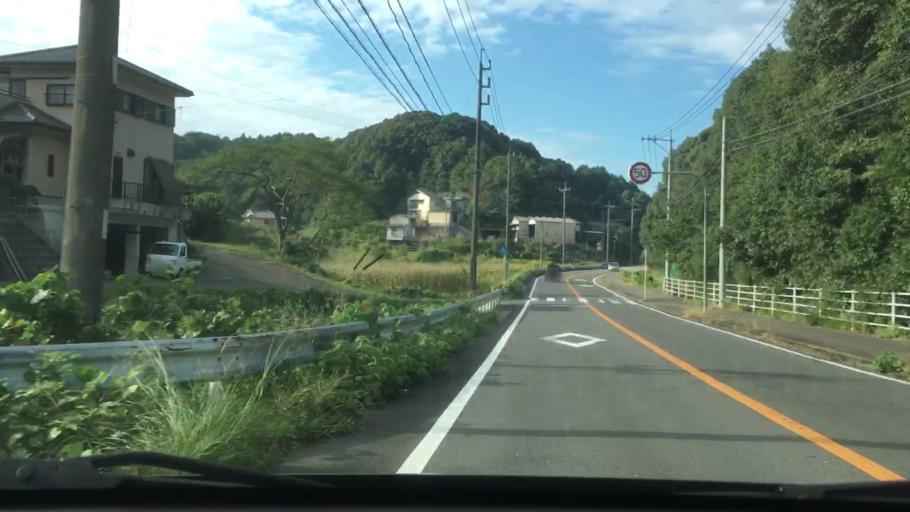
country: JP
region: Nagasaki
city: Togitsu
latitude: 32.9434
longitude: 129.6581
